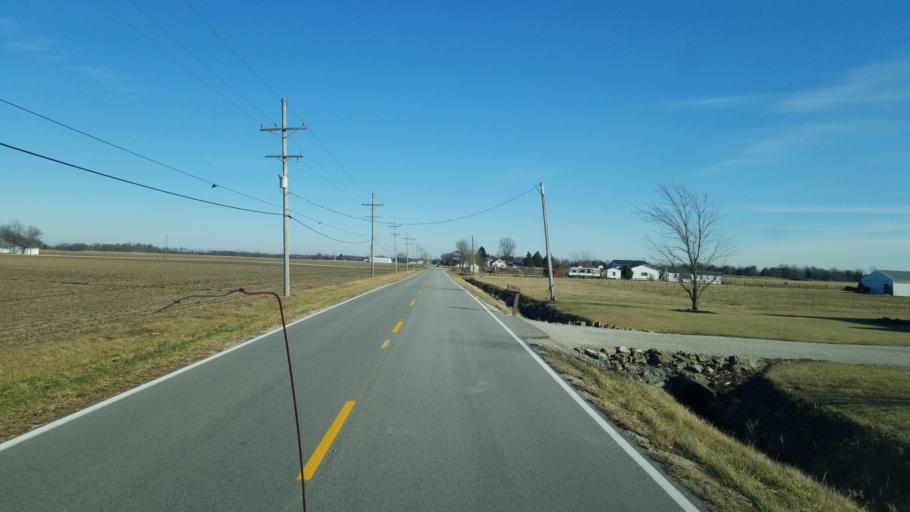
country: US
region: Ohio
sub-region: Sandusky County
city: Stony Prairie
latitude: 41.3491
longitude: -83.2031
